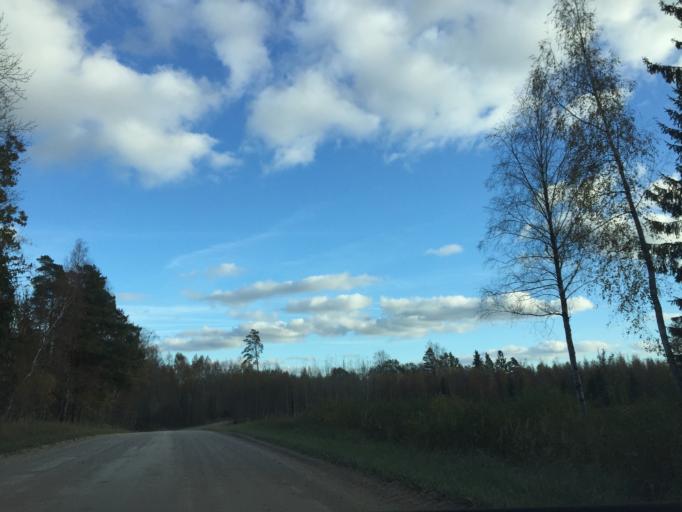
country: LV
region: Tukuma Rajons
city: Tukums
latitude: 56.9627
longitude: 22.9746
